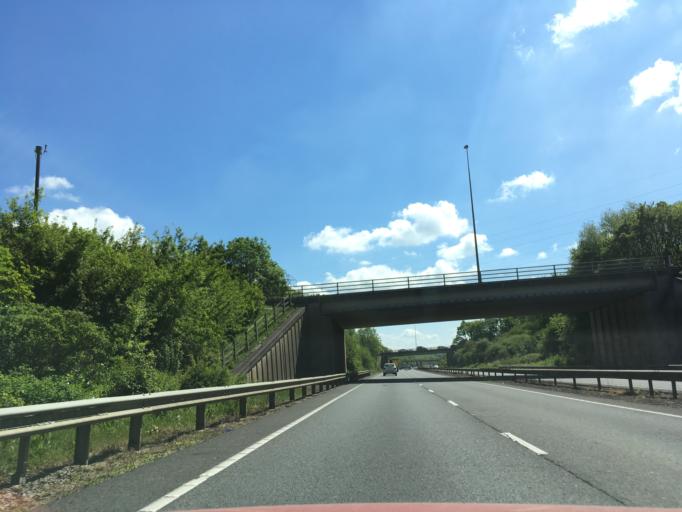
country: GB
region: England
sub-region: Milton Keynes
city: Bradwell
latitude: 52.0477
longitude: -0.8065
